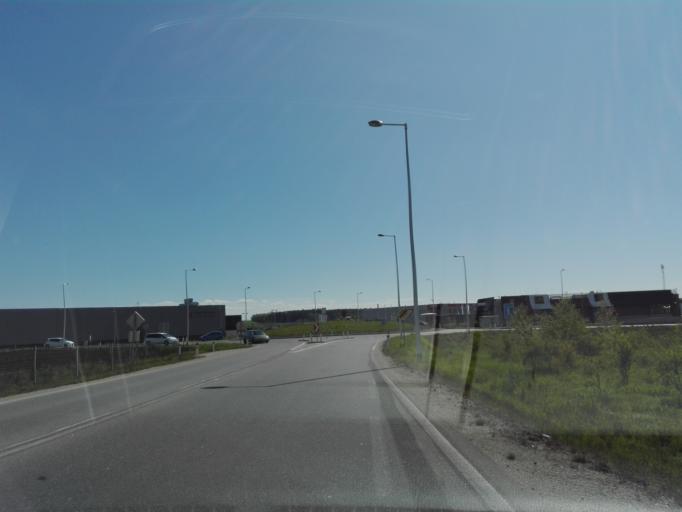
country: AT
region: Upper Austria
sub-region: Politischer Bezirk Urfahr-Umgebung
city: Engerwitzdorf
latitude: 48.3604
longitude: 14.4817
